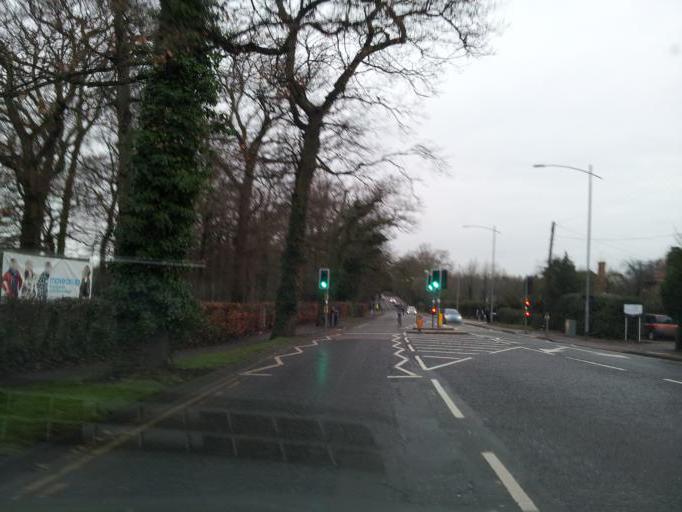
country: GB
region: England
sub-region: Cambridgeshire
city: Cambridge
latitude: 52.1792
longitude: 0.1352
